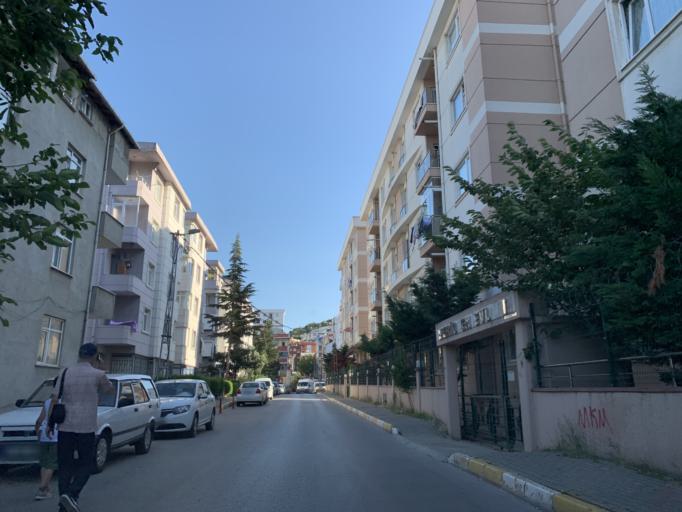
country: TR
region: Istanbul
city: Pendik
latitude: 40.8958
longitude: 29.2568
